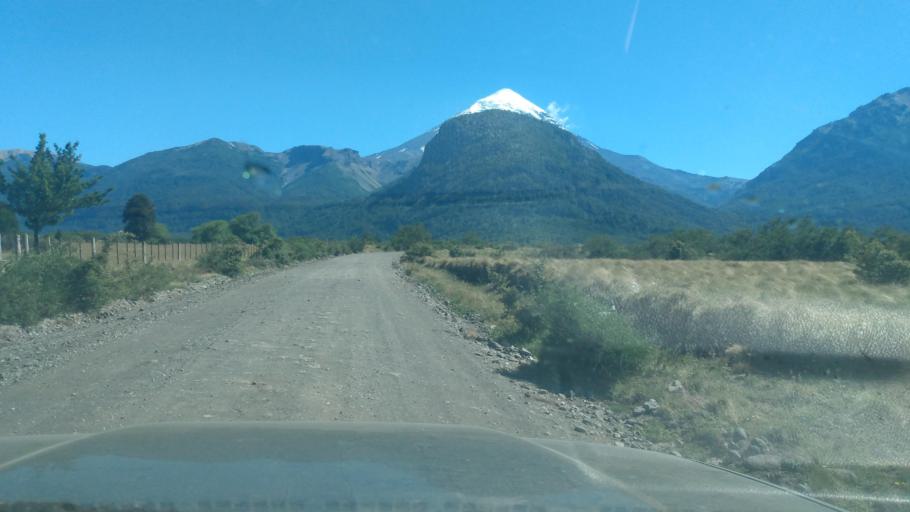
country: AR
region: Neuquen
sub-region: Departamento de Lacar
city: San Martin de los Andes
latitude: -39.7436
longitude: -71.5227
